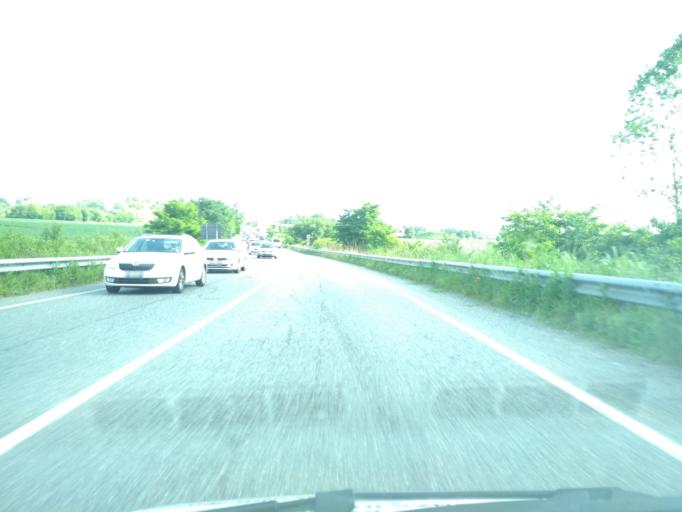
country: IT
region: Piedmont
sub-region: Provincia di Torino
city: Pasta
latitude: 45.0245
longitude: 7.5516
